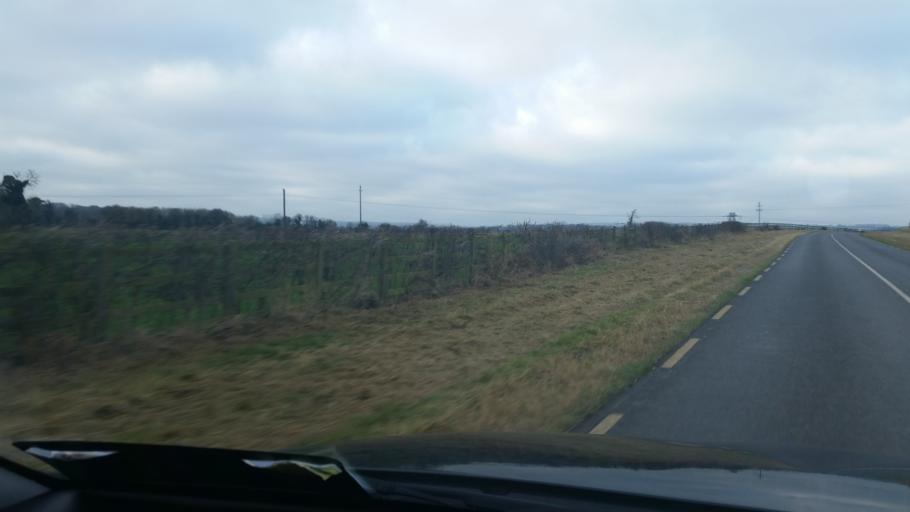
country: IE
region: Leinster
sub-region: Lu
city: Tullyallen
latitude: 53.7098
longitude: -6.4118
